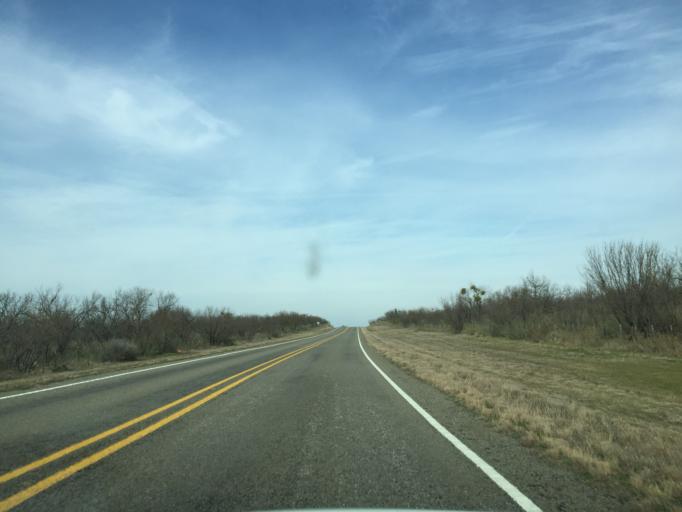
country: US
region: Texas
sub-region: Llano County
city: Llano
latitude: 30.5346
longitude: -98.7078
